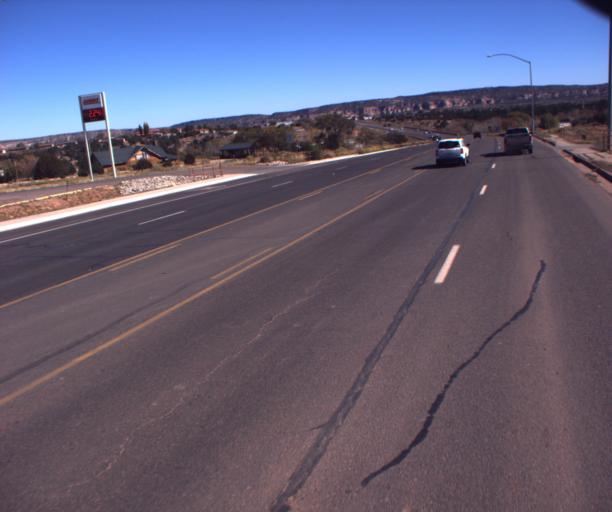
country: US
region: Arizona
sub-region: Apache County
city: Saint Michaels
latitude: 35.6564
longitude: -109.1086
